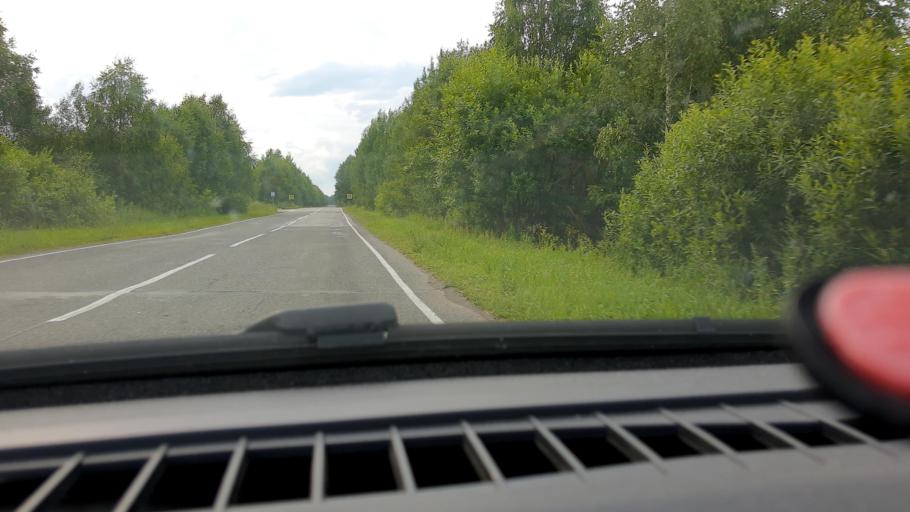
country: RU
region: Nizjnij Novgorod
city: Neklyudovo
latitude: 56.5125
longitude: 43.9457
